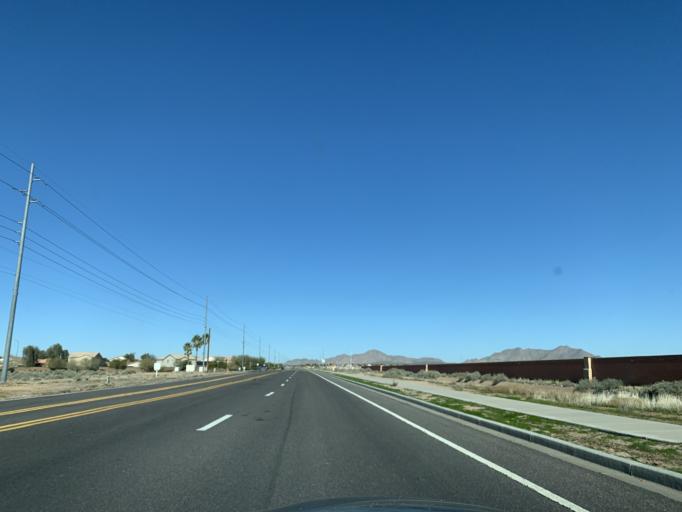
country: US
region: Arizona
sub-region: Pinal County
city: Casa Grande
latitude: 32.9258
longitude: -111.7224
